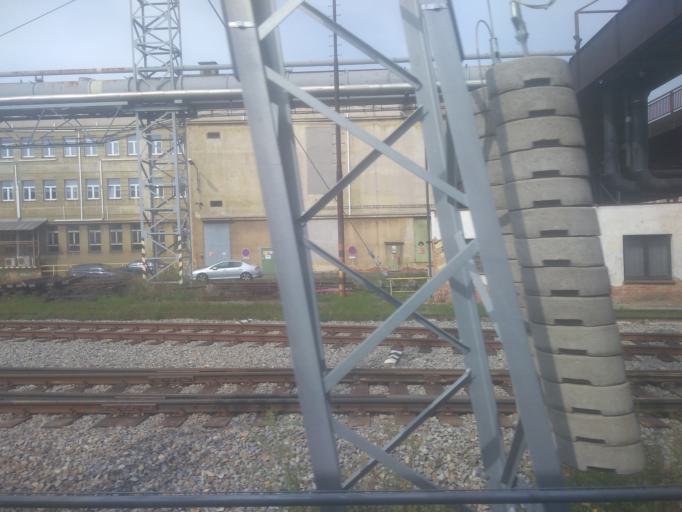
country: CZ
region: Plzensky
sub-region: Okres Plzen-Mesto
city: Pilsen
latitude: 49.7415
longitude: 13.3610
